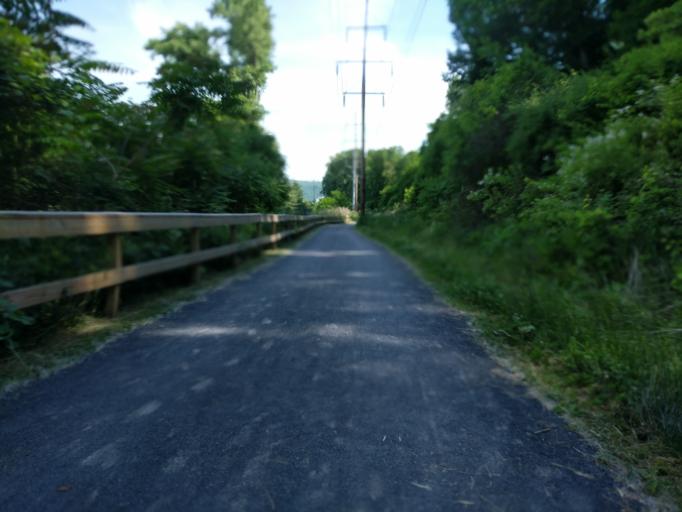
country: US
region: New York
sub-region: Tompkins County
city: Ithaca
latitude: 42.4488
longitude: -76.5159
